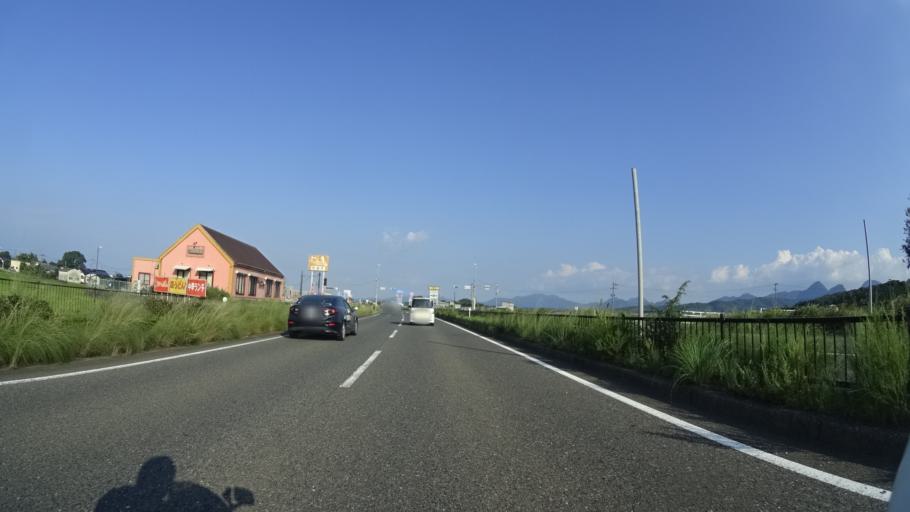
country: JP
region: Fukuoka
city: Nakatsu
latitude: 33.5516
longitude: 131.2662
